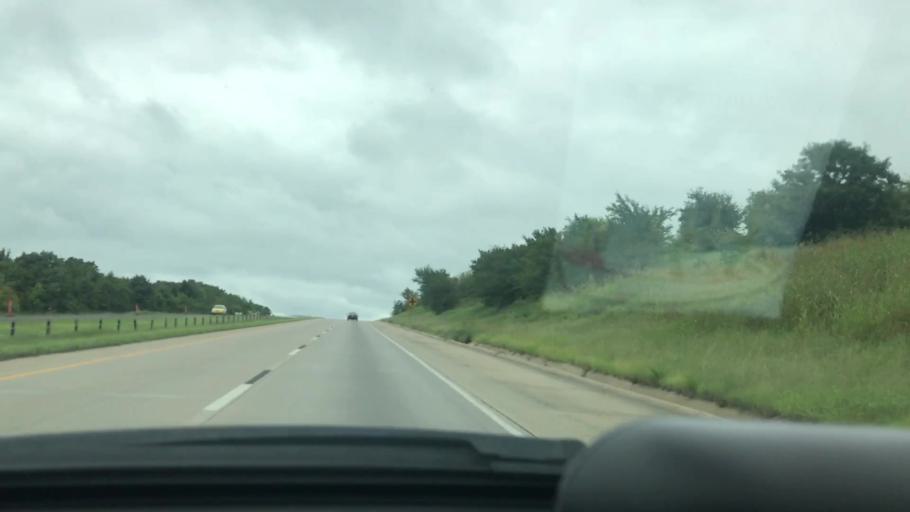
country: US
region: Oklahoma
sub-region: Pittsburg County
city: Krebs
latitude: 34.9668
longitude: -95.7241
